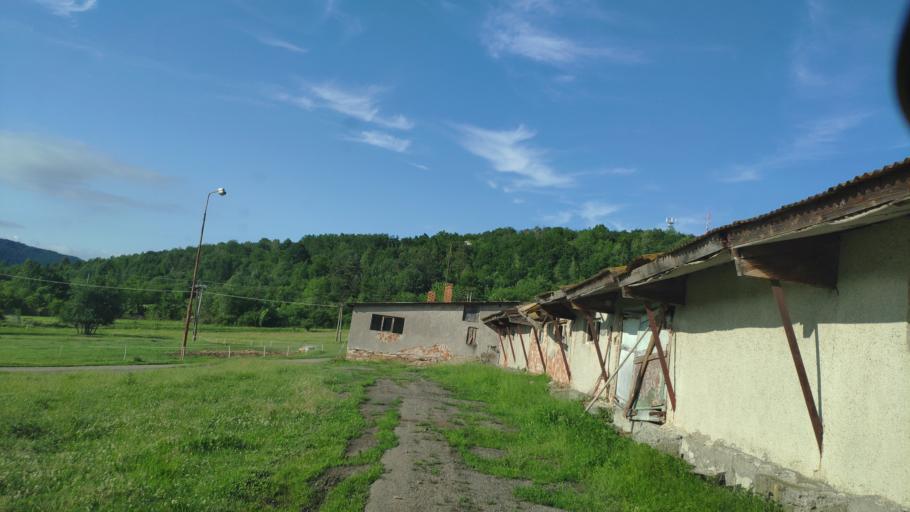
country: SK
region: Presovsky
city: Vranov nad Topl'ou
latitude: 48.8255
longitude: 21.5802
